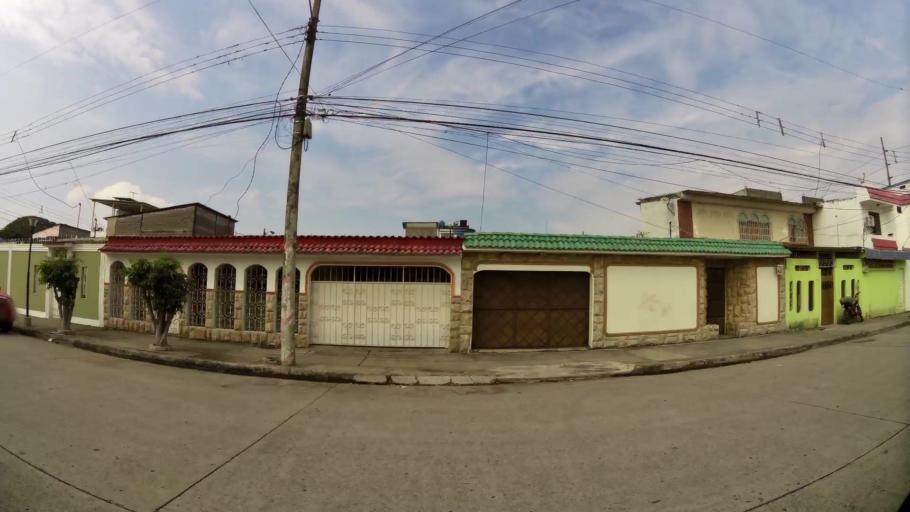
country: EC
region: Guayas
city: Guayaquil
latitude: -2.2492
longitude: -79.9013
